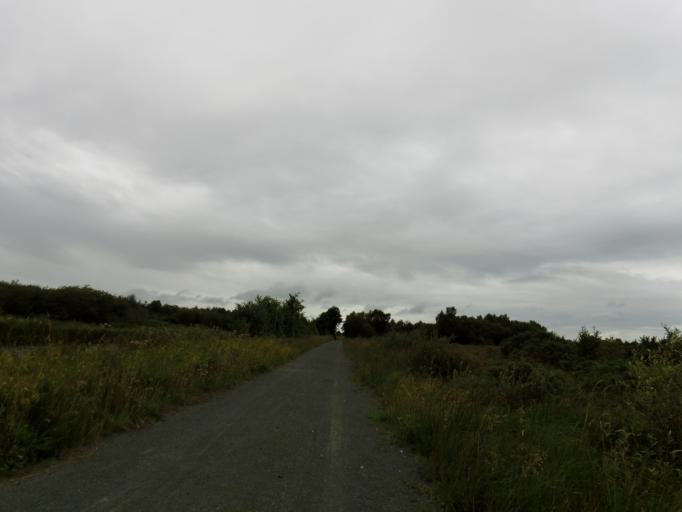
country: IE
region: Leinster
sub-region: An Iarmhi
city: Moate
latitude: 53.5871
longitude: -7.6287
